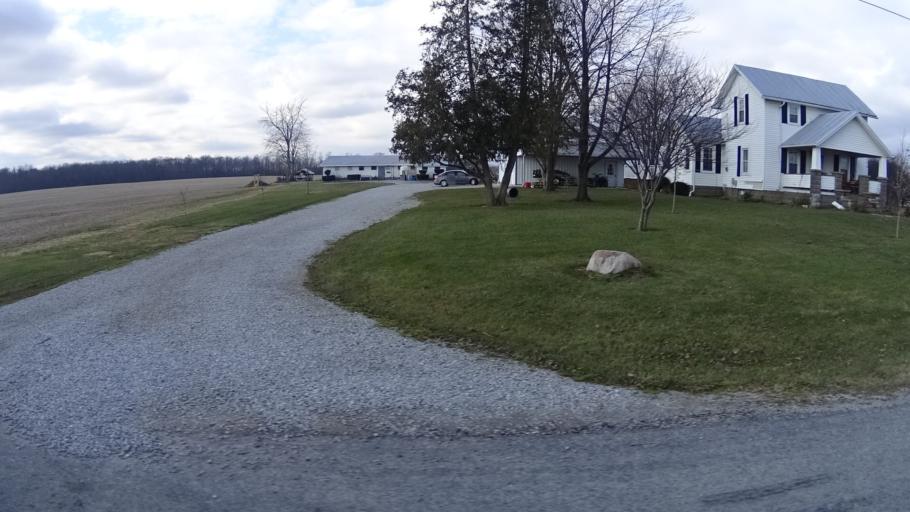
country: US
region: Ohio
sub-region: Lorain County
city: Camden
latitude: 41.2160
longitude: -82.2754
